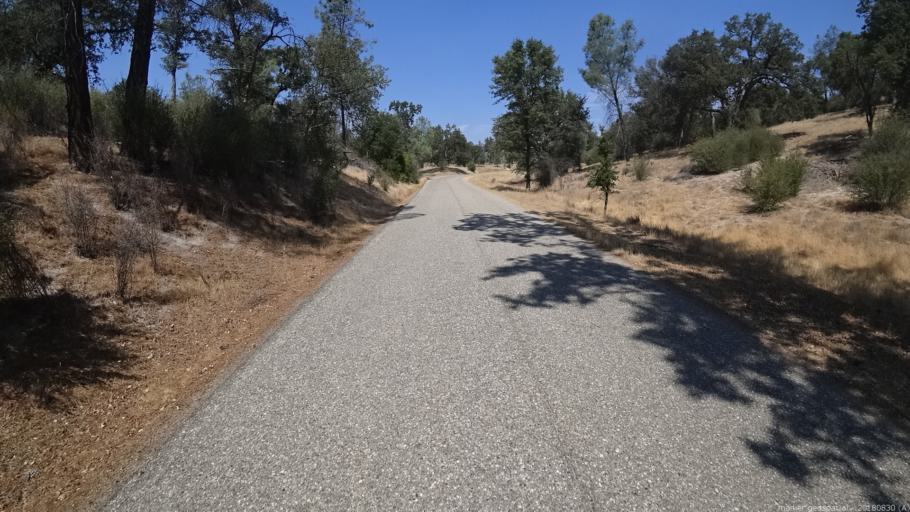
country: US
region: California
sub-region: Monterey County
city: King City
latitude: 35.9895
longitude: -121.2618
